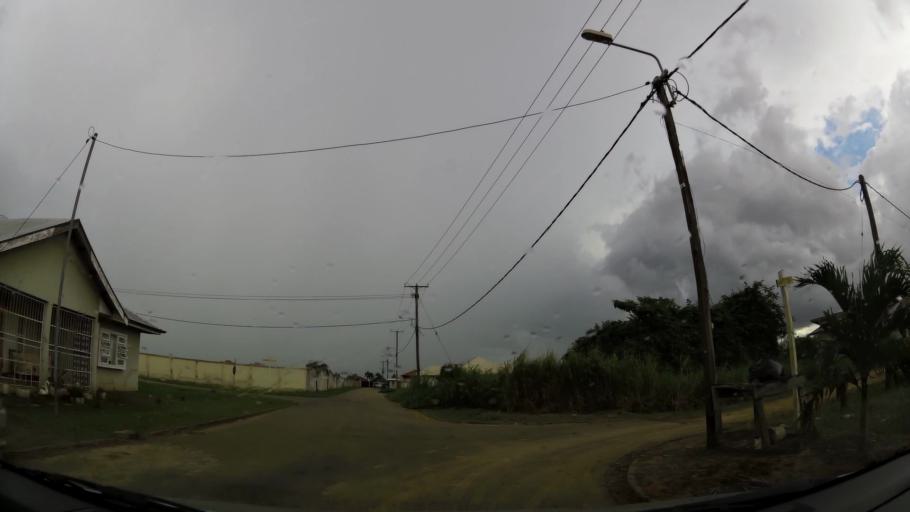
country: SR
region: Commewijne
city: Nieuw Amsterdam
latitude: 5.8509
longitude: -55.1132
